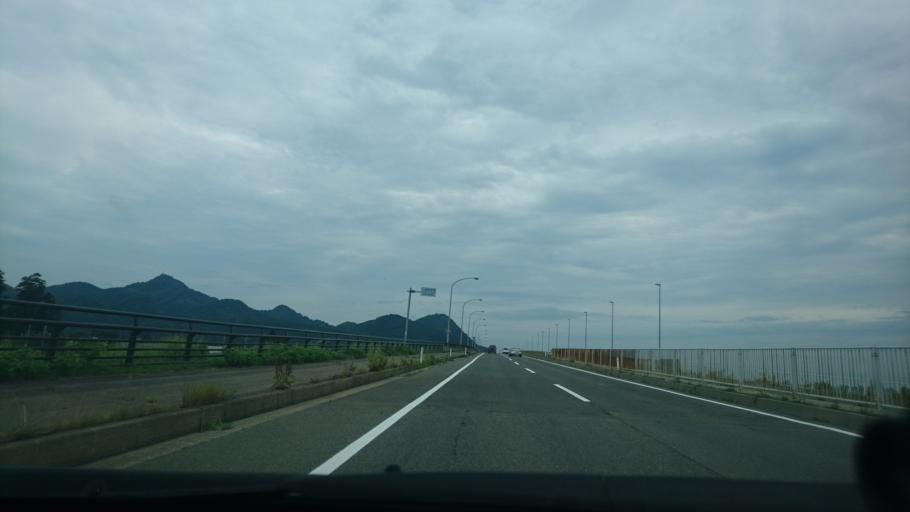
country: JP
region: Akita
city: Omagari
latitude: 39.4757
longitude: 140.4717
